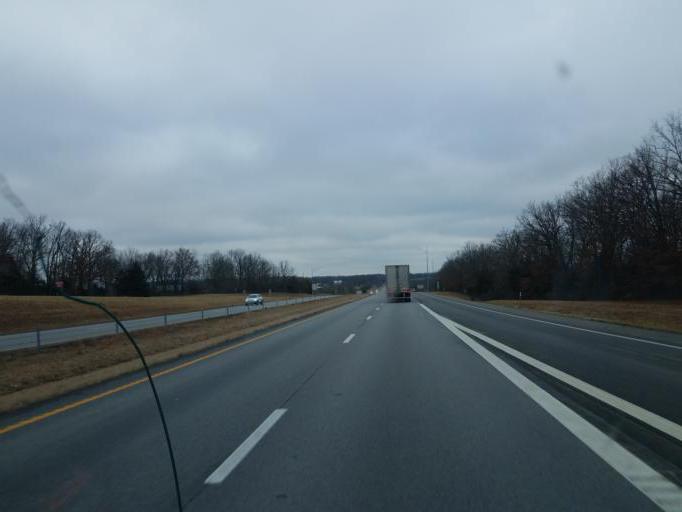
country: US
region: Missouri
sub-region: Webster County
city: Marshfield
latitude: 37.4720
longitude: -92.8583
